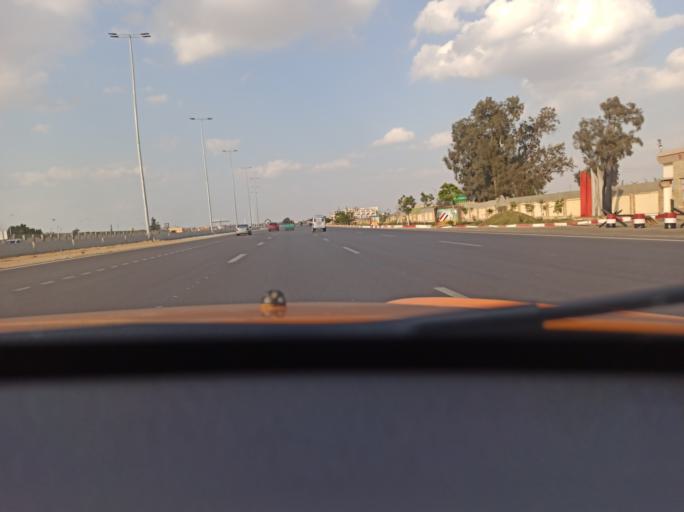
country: EG
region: Al Isma'iliyah
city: Ismailia
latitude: 30.6004
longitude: 32.2073
